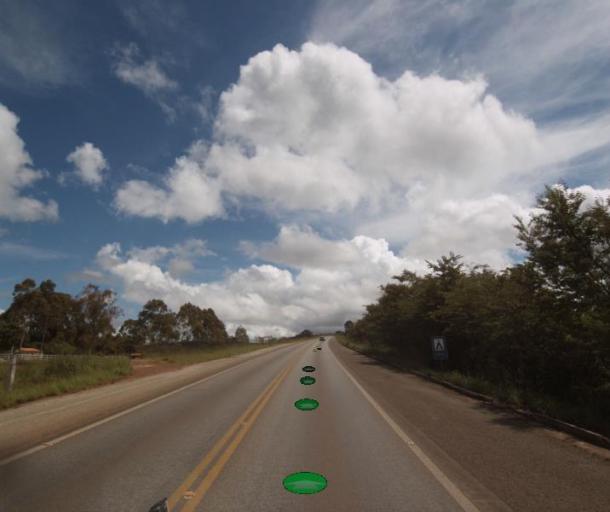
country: BR
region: Federal District
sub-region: Brasilia
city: Brasilia
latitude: -15.7432
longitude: -48.3701
